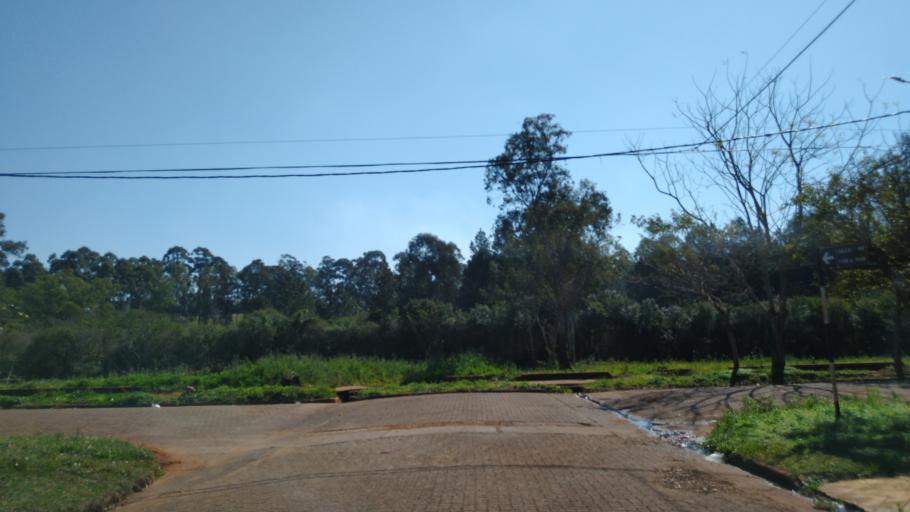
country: AR
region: Misiones
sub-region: Departamento de Capital
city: Posadas
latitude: -27.4102
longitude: -55.9592
